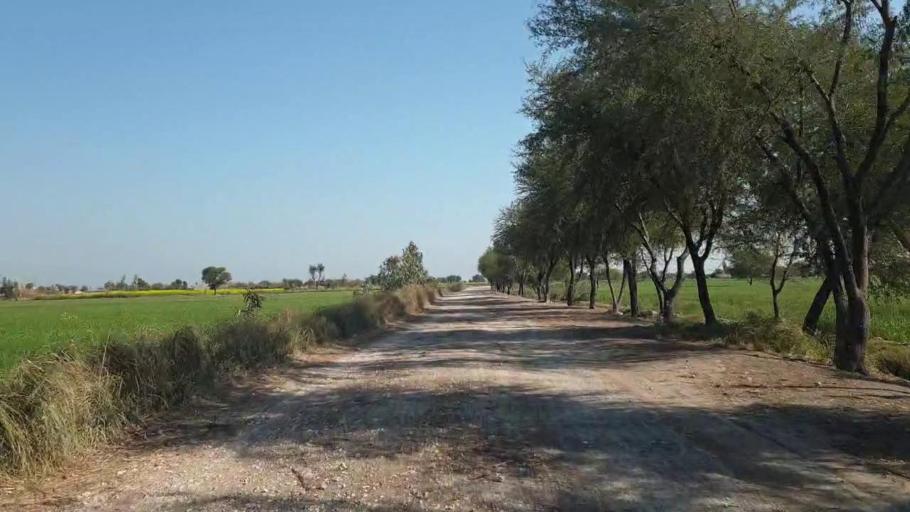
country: PK
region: Sindh
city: Shahdadpur
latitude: 25.9785
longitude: 68.6750
